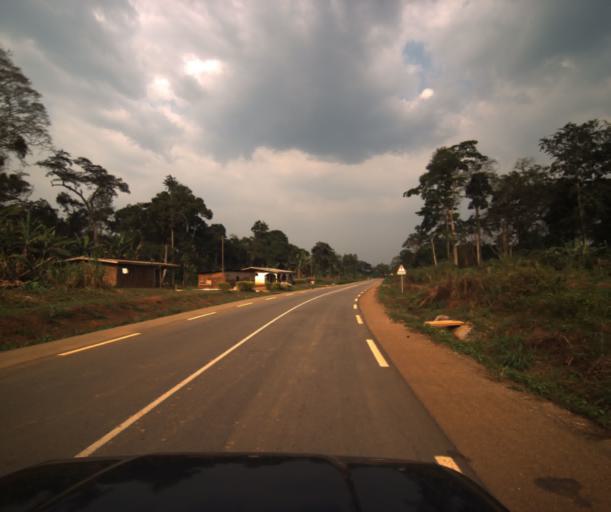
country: CM
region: Centre
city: Mbankomo
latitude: 3.7431
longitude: 11.3958
